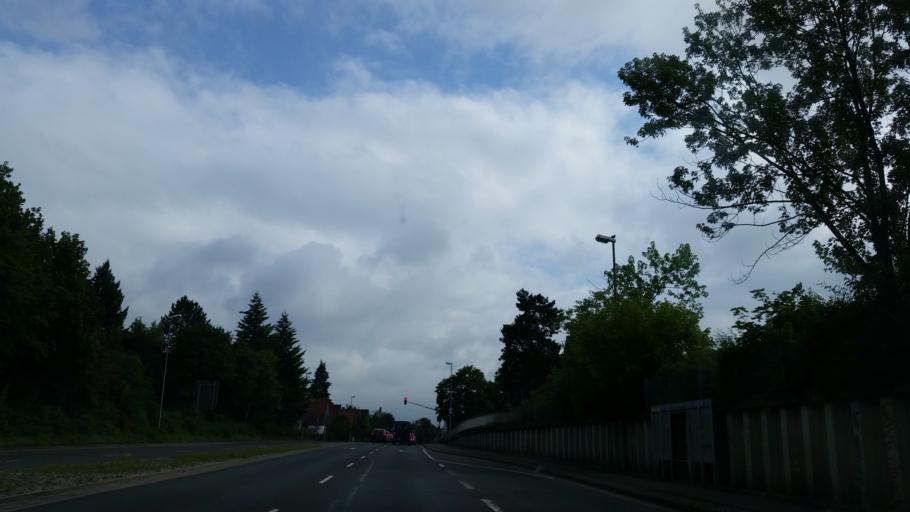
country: DE
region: Lower Saxony
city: Peine
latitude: 52.3358
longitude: 10.2373
